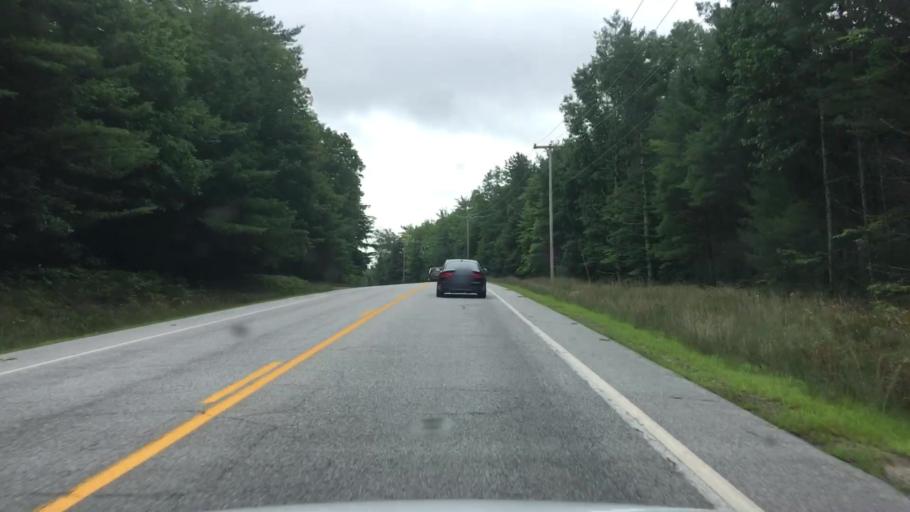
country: US
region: Maine
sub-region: Oxford County
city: Hiram
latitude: 43.8489
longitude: -70.7887
